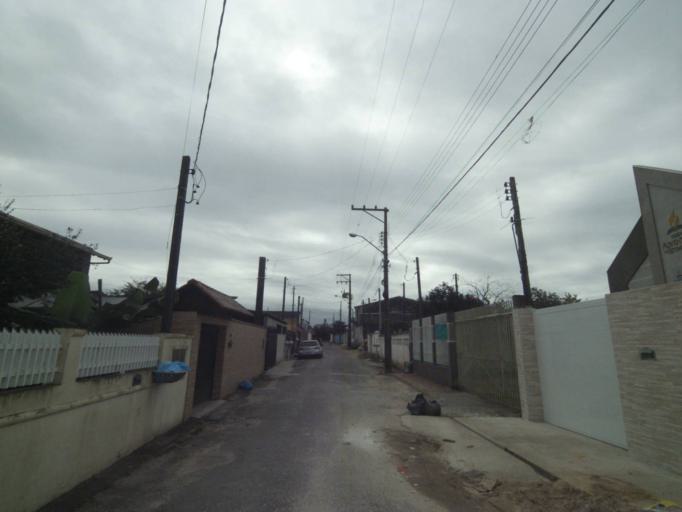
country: BR
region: Parana
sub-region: Paranagua
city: Paranagua
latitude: -25.5185
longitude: -48.5313
